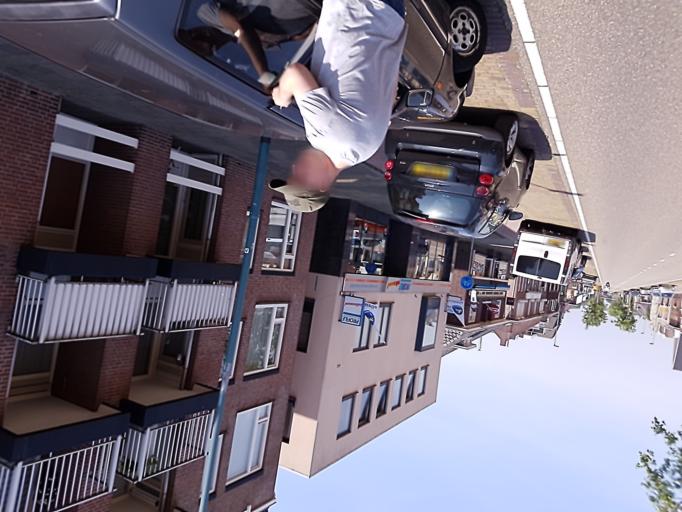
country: NL
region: North Brabant
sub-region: Gemeente Valkenswaard
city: Valkenswaard
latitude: 51.3563
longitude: 5.4612
